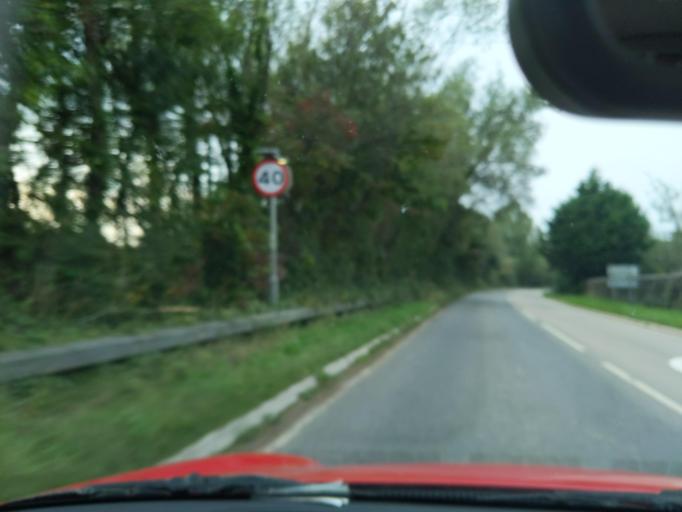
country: GB
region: England
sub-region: Devon
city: Okehampton
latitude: 50.8189
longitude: -4.0747
